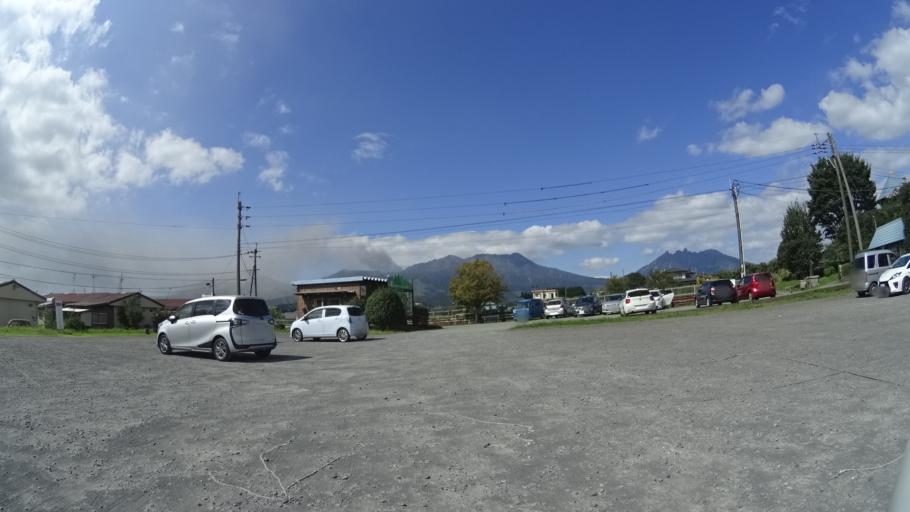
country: JP
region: Kumamoto
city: Aso
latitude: 32.8132
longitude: 131.1223
